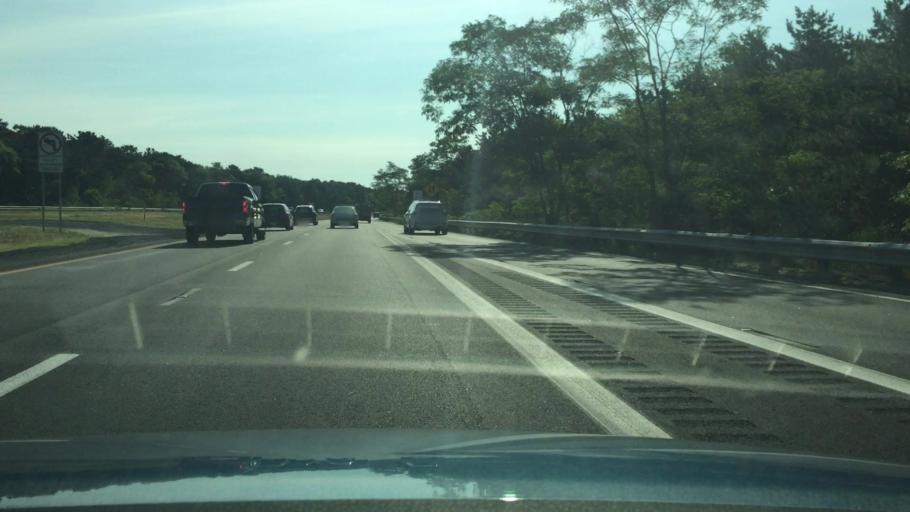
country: US
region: Massachusetts
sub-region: Barnstable County
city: South Dennis
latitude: 41.6992
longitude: -70.1476
